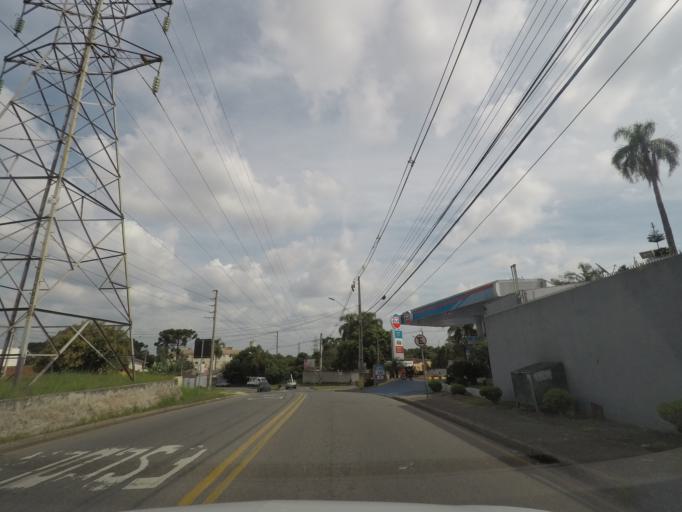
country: BR
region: Parana
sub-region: Pinhais
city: Pinhais
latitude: -25.4828
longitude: -49.2132
